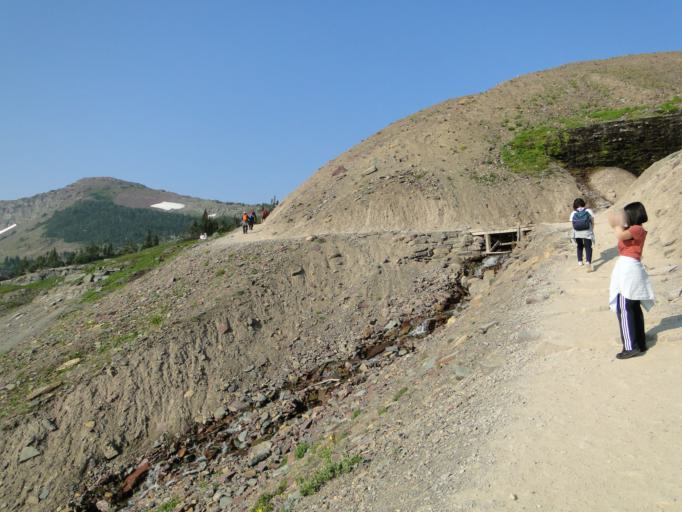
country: US
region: Montana
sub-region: Flathead County
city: Columbia Falls
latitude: 48.6901
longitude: -113.7329
